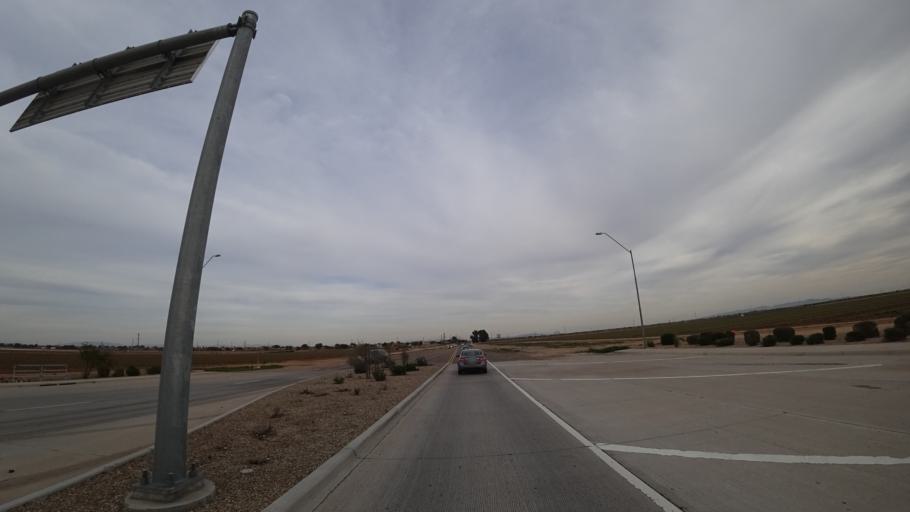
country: US
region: Arizona
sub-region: Maricopa County
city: Citrus Park
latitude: 33.6097
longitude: -112.4168
